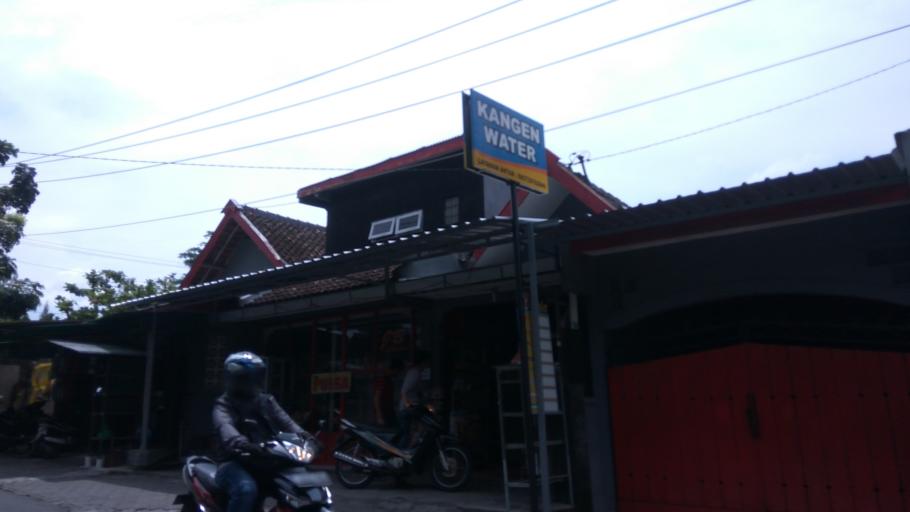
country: ID
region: Daerah Istimewa Yogyakarta
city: Depok
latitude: -7.7460
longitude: 110.4171
